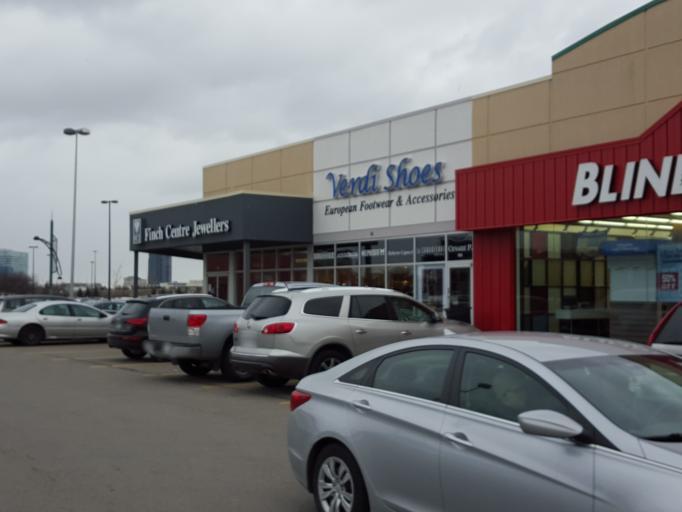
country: CA
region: Ontario
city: Concord
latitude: 43.7854
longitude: -79.5447
